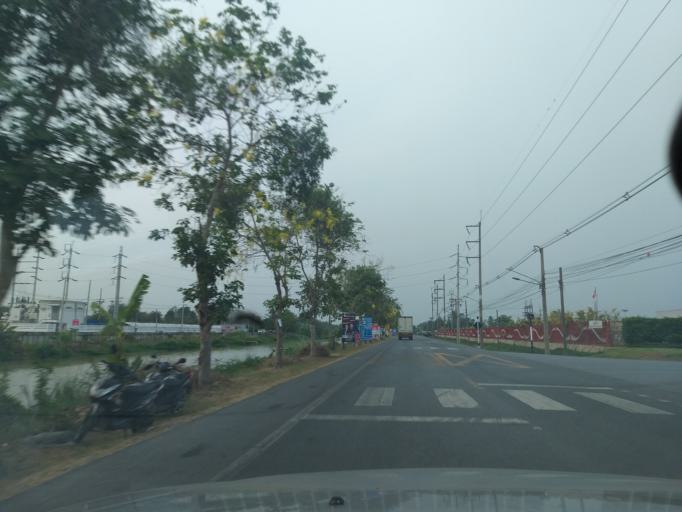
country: TH
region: Pathum Thani
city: Ban Lam Luk Ka
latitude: 13.9936
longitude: 100.8952
